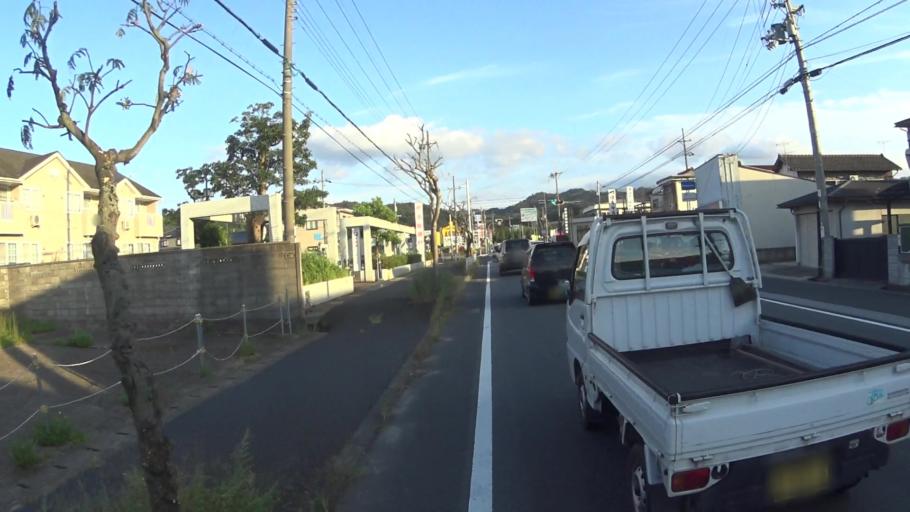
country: JP
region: Kyoto
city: Miyazu
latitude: 35.5851
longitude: 135.0984
